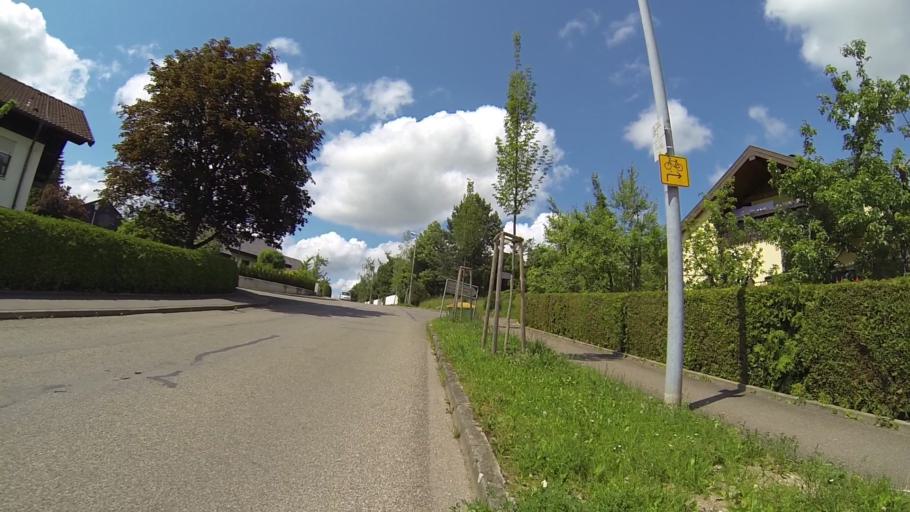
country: DE
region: Baden-Wuerttemberg
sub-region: Regierungsbezirk Stuttgart
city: Waldstetten
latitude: 48.7682
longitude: 9.8320
